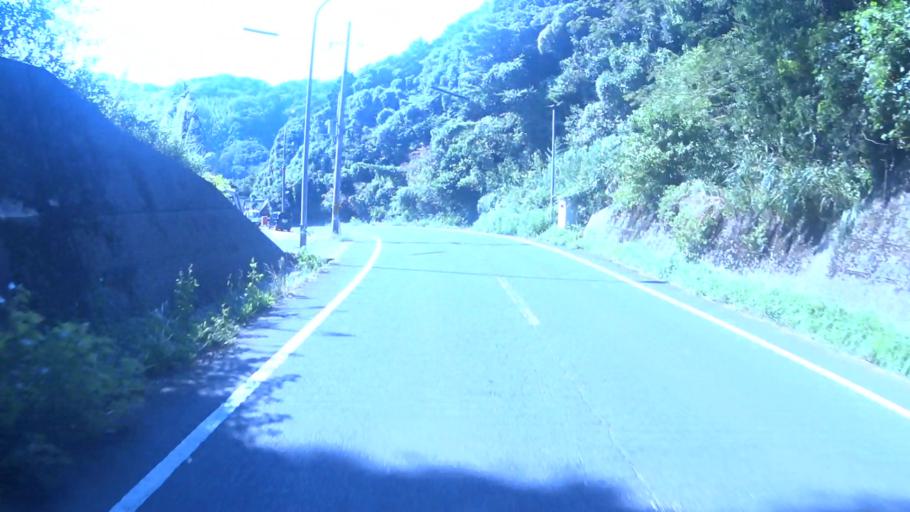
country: JP
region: Kyoto
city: Miyazu
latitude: 35.6775
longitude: 135.2907
